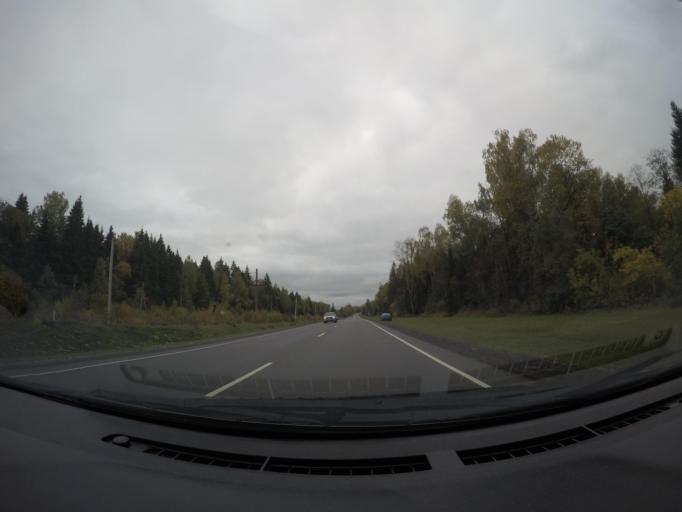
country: RU
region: Moskovskaya
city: Ruza
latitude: 55.7233
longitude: 36.2147
